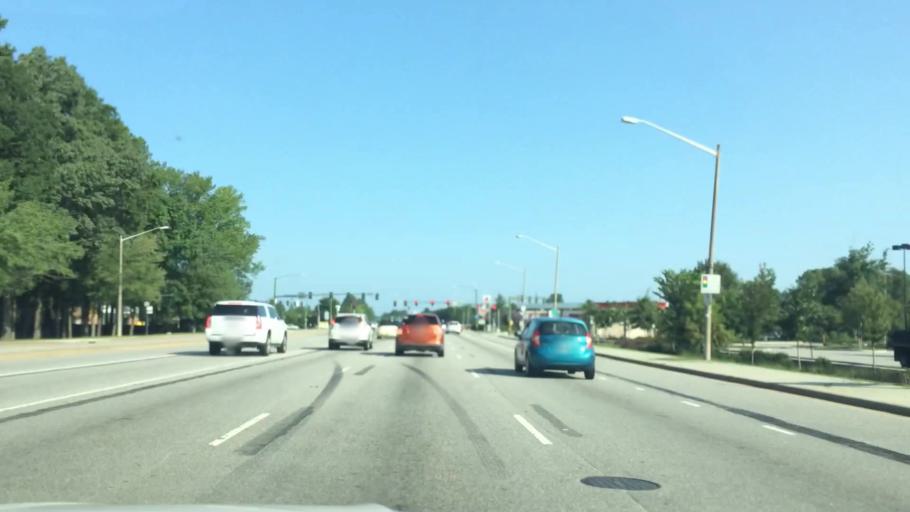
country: US
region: Virginia
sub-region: York County
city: Yorktown
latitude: 37.1035
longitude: -76.4930
